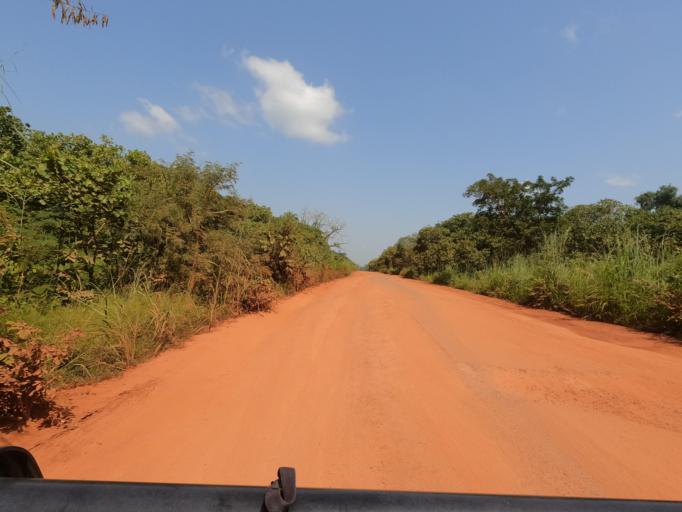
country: GW
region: Oio
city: Bissora
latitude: 12.3182
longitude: -15.7582
